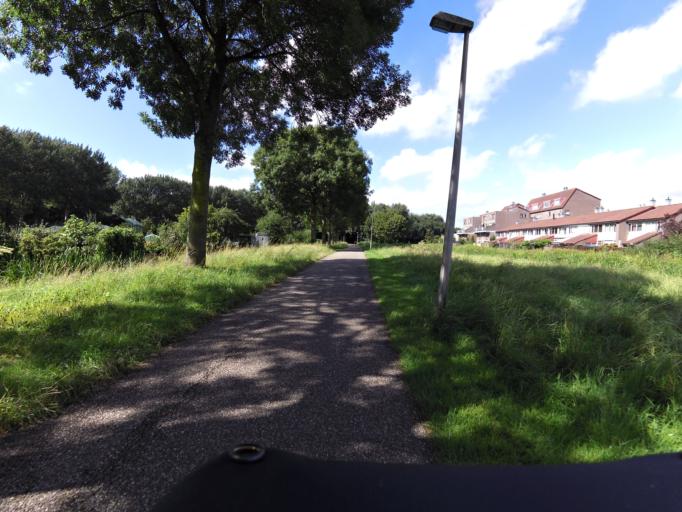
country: NL
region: South Holland
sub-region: Gemeente Spijkenisse
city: Spijkenisse
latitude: 51.8425
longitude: 4.3127
